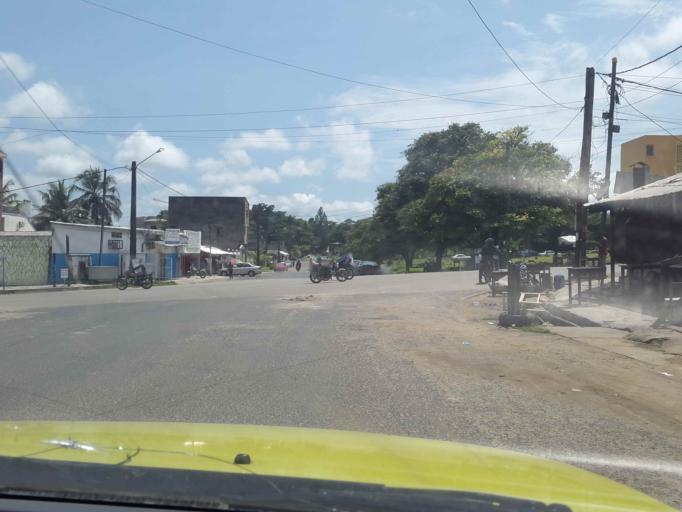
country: CM
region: Littoral
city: Douala
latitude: 4.0866
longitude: 9.7384
